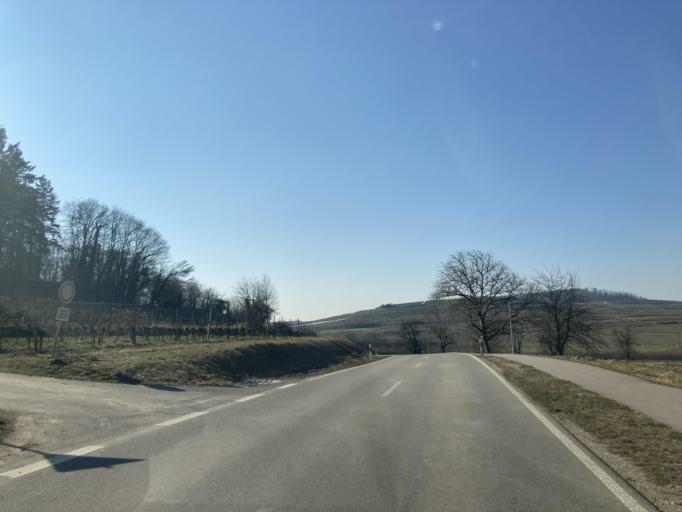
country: DE
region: Baden-Wuerttemberg
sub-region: Freiburg Region
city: Vogtsburg
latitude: 48.1052
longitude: 7.6183
